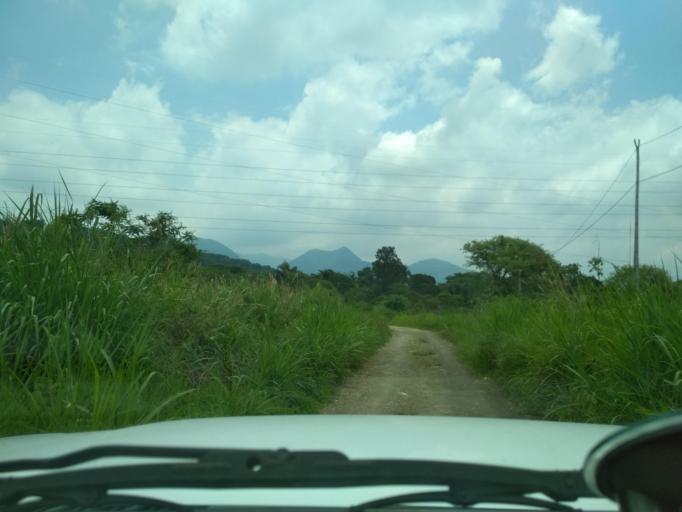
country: MX
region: Veracruz
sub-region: Ixtaczoquitlan
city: Buenavista
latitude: 18.8849
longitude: -97.0628
